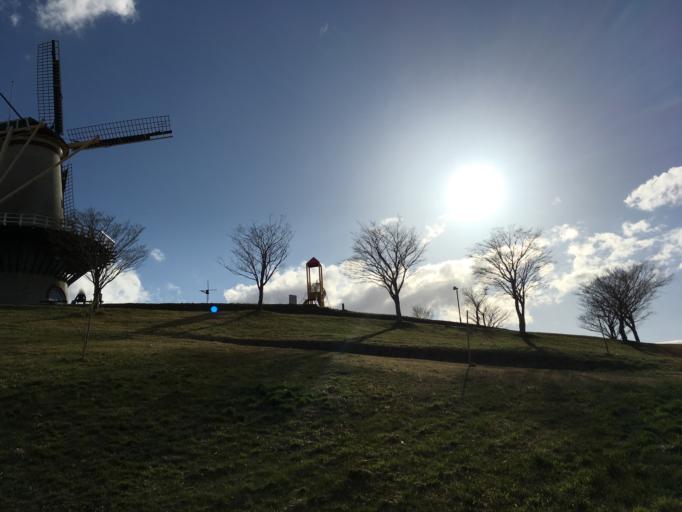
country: JP
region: Miyagi
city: Wakuya
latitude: 38.6902
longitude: 141.1369
